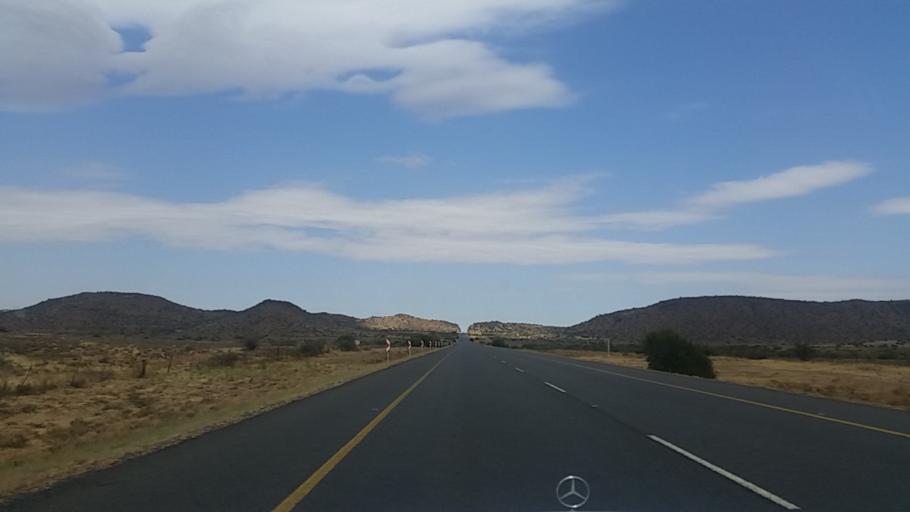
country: ZA
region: Northern Cape
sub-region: Pixley ka Seme District Municipality
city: Colesberg
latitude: -30.6365
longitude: 25.2362
